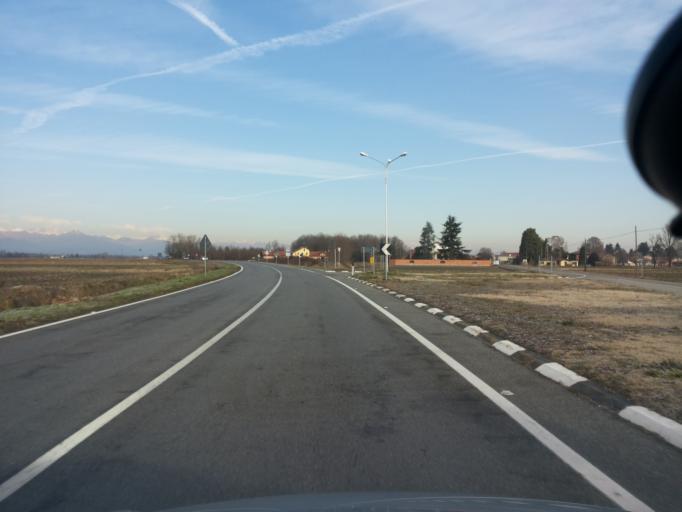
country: IT
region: Piedmont
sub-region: Provincia di Vercelli
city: Albano Vercellese
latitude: 45.4199
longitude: 8.3797
